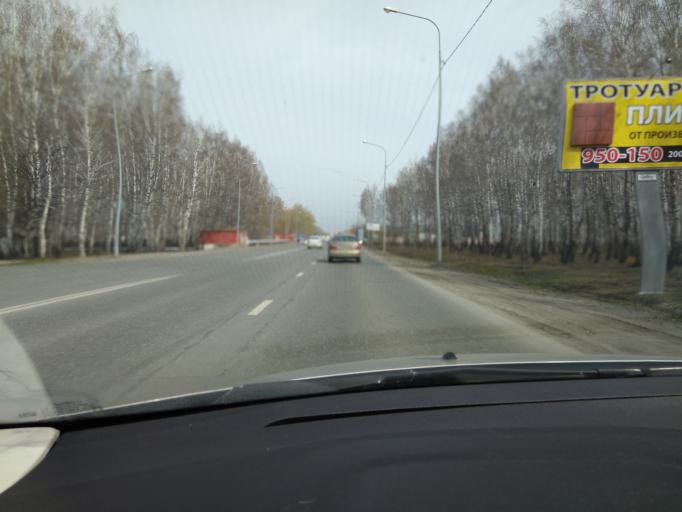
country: RU
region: Tjumen
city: Melioratorov
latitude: 57.1810
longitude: 65.5916
